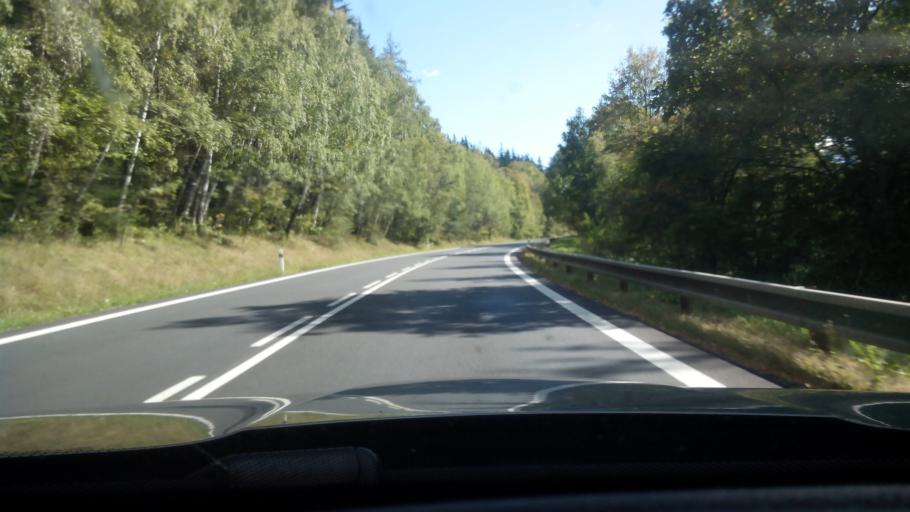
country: CZ
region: Jihocesky
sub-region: Okres Prachatice
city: Zdikov
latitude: 49.0732
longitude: 13.7112
